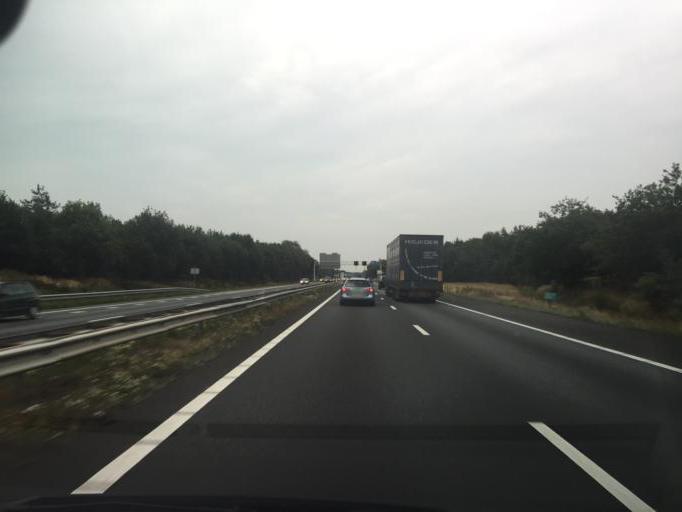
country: NL
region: North Brabant
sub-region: Gemeente Eindhoven
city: De Doornakkers
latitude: 51.4049
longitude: 5.5222
